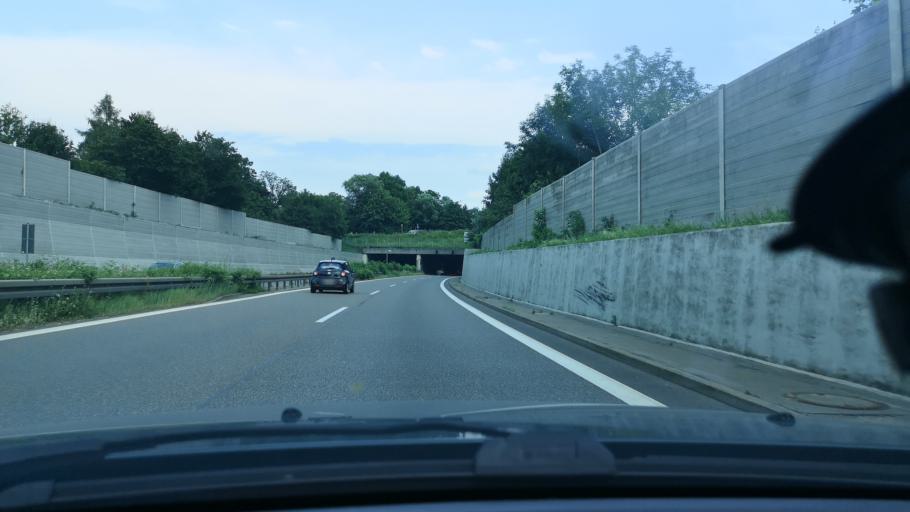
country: DE
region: Baden-Wuerttemberg
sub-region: Regierungsbezirk Stuttgart
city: Goeppingen
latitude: 48.6998
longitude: 9.6411
